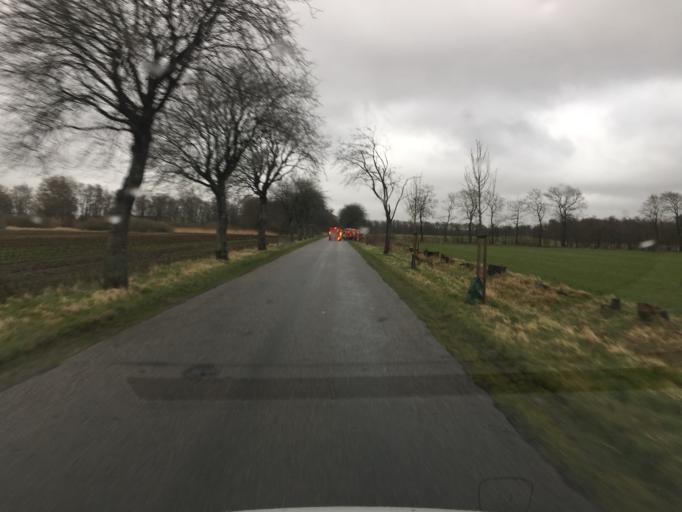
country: DK
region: South Denmark
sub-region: Aabenraa Kommune
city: Tinglev
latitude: 54.9020
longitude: 9.3090
